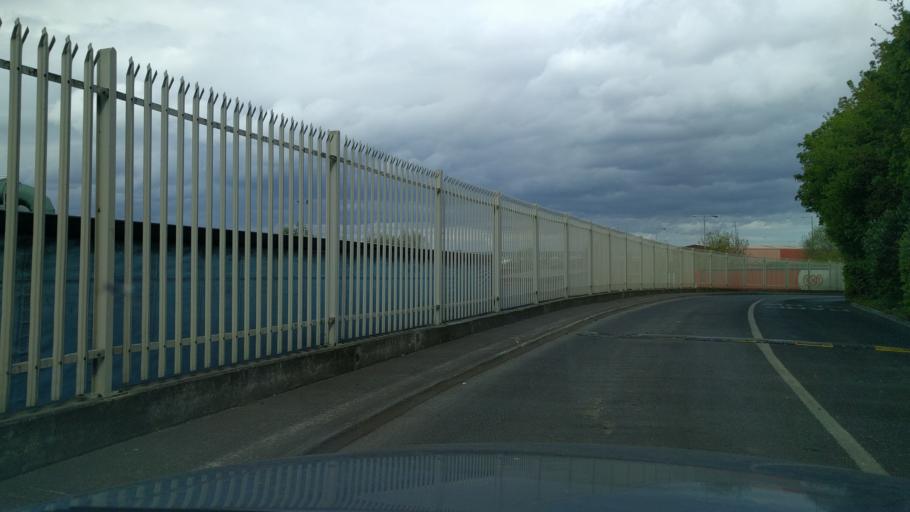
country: IE
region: Leinster
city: Crumlin
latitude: 53.3099
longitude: -6.3460
